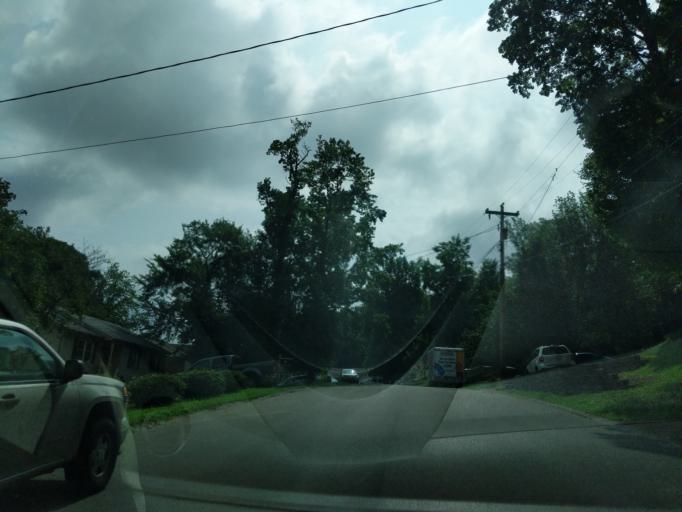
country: US
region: Tennessee
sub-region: Davidson County
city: Lakewood
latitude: 36.1859
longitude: -86.6051
